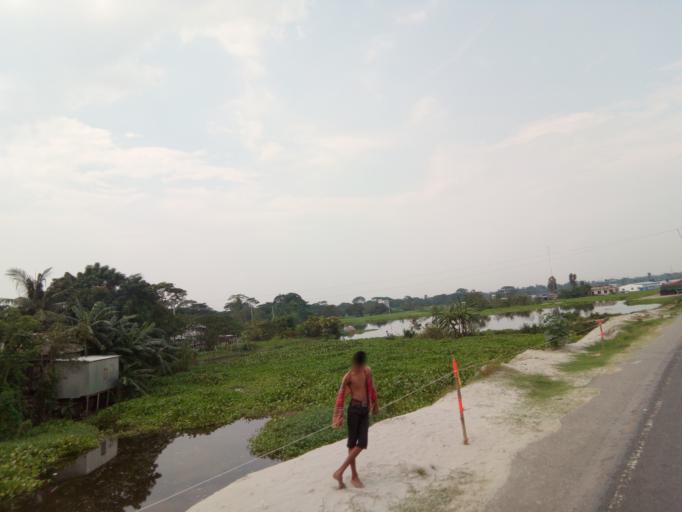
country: BD
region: Dhaka
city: Dohar
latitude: 23.5178
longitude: 90.2794
